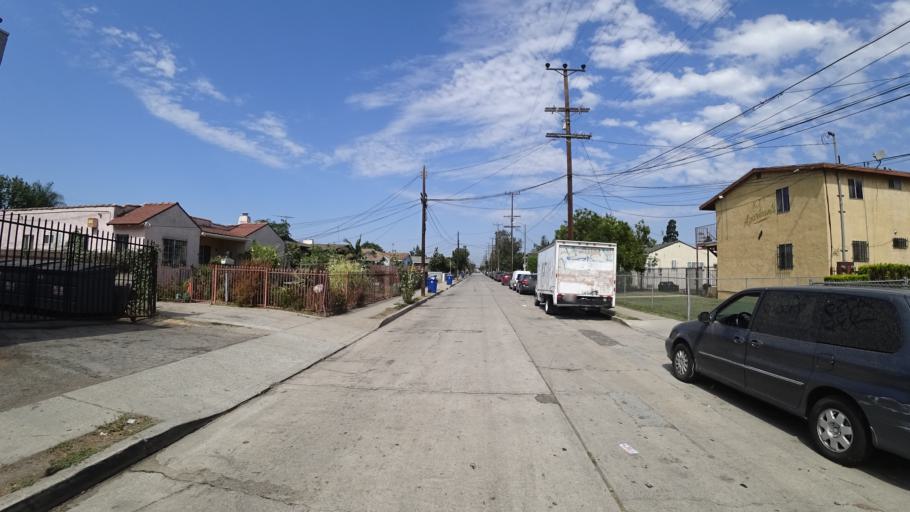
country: US
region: California
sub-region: Los Angeles County
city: Westmont
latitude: 33.9551
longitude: -118.2831
